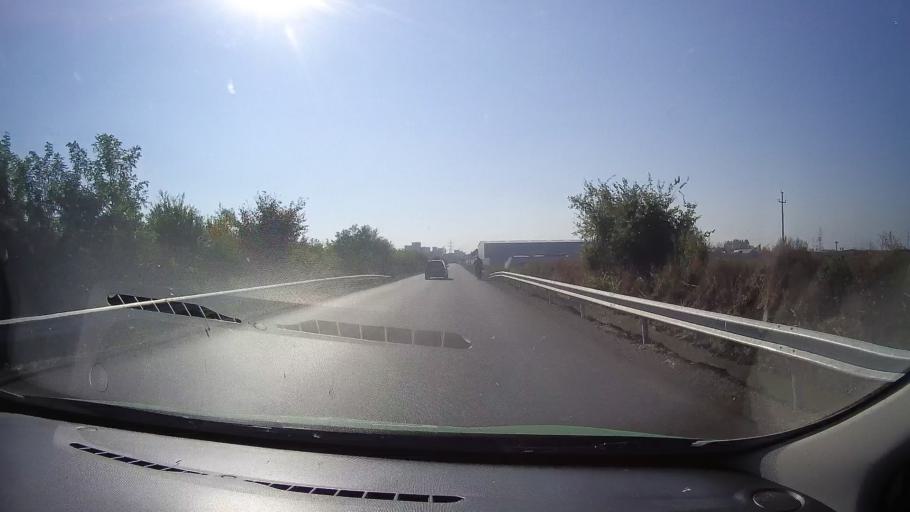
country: RO
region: Satu Mare
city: Carei
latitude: 47.7064
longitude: 22.4673
